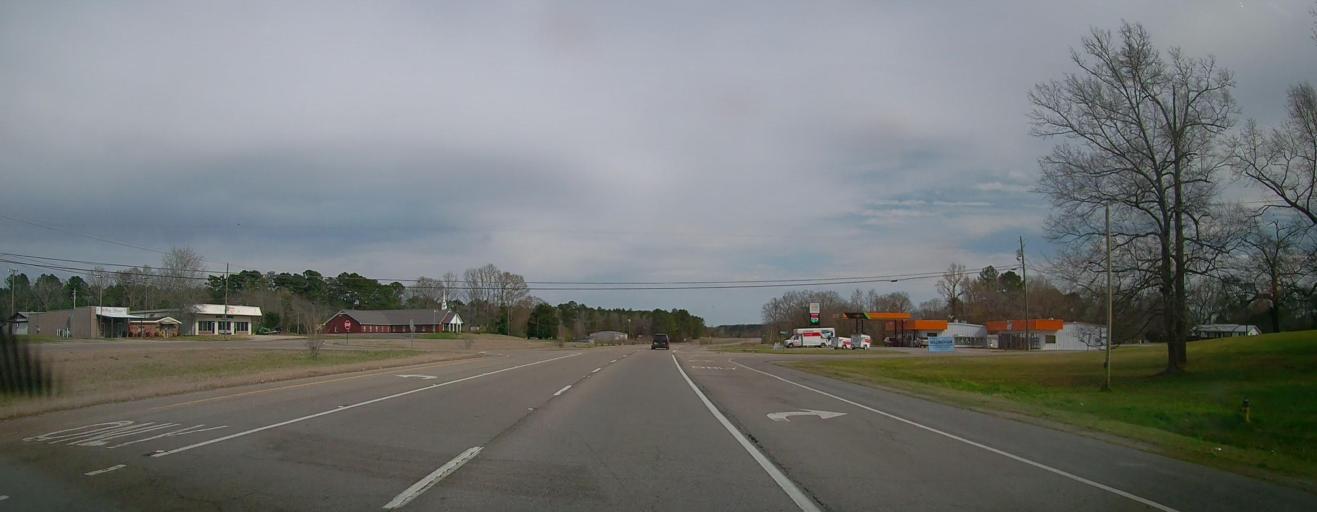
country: US
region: Alabama
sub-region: Walker County
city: Cordova
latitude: 33.8013
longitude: -87.1178
